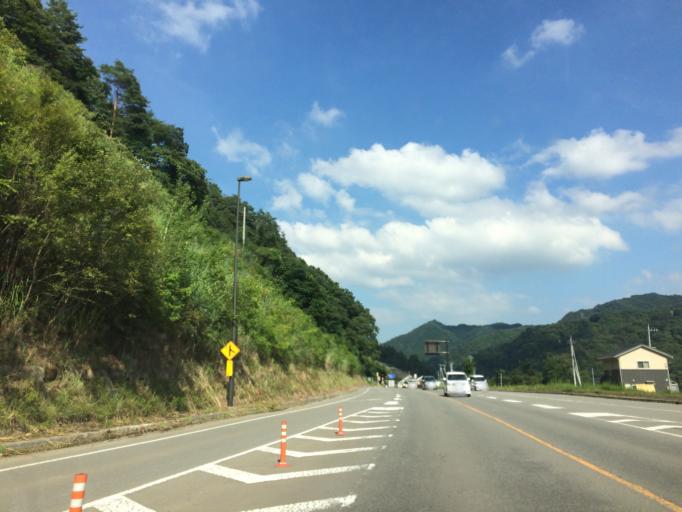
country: JP
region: Gunma
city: Nakanojomachi
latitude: 36.5573
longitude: 138.7049
